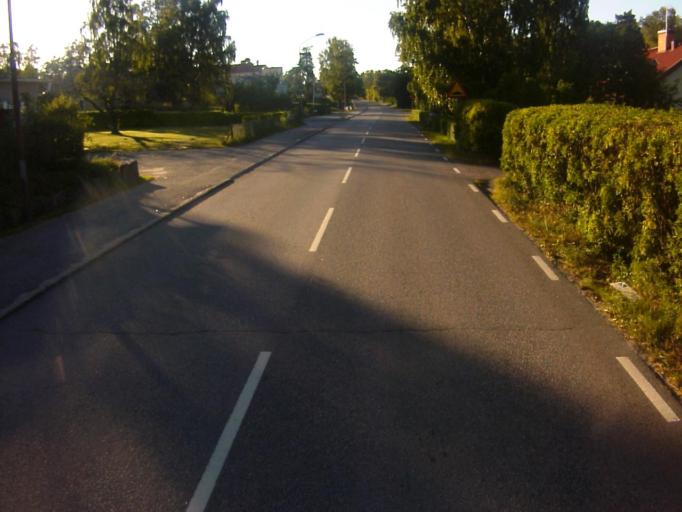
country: SE
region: Soedermanland
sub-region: Eskilstuna Kommun
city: Hallbybrunn
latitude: 59.3912
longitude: 16.4290
